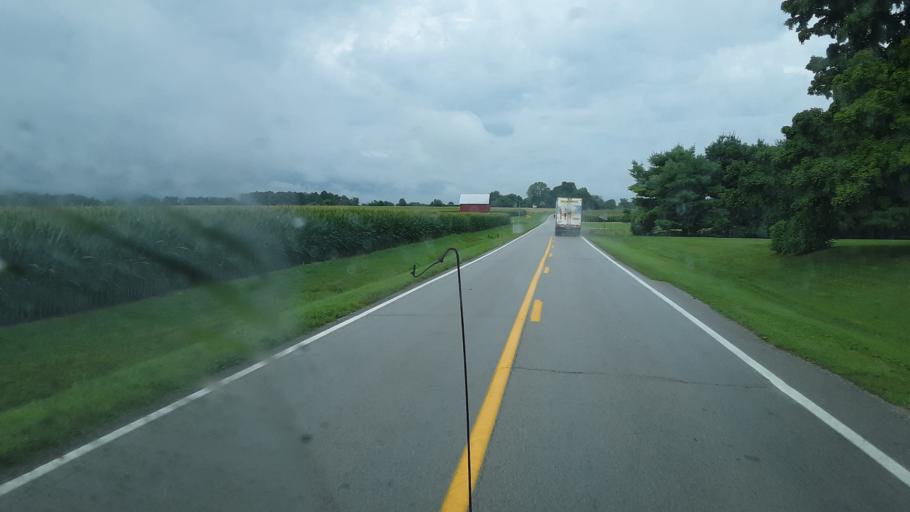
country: US
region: Kentucky
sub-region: Logan County
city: Russellville
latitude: 36.7827
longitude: -86.9996
